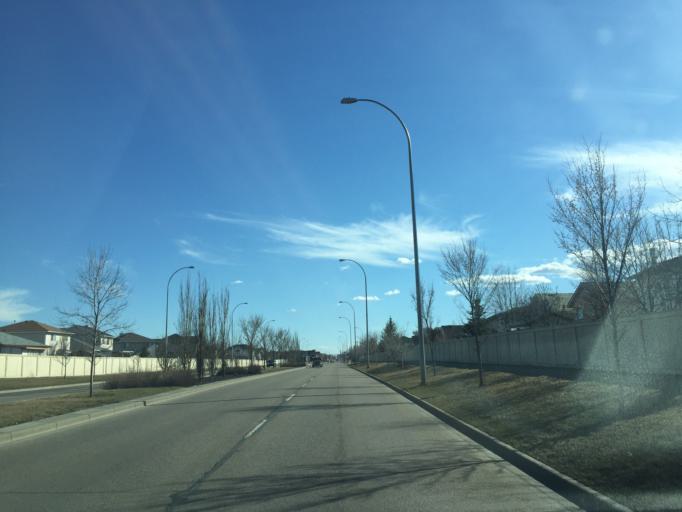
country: CA
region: Alberta
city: Airdrie
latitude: 51.2974
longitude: -114.0254
